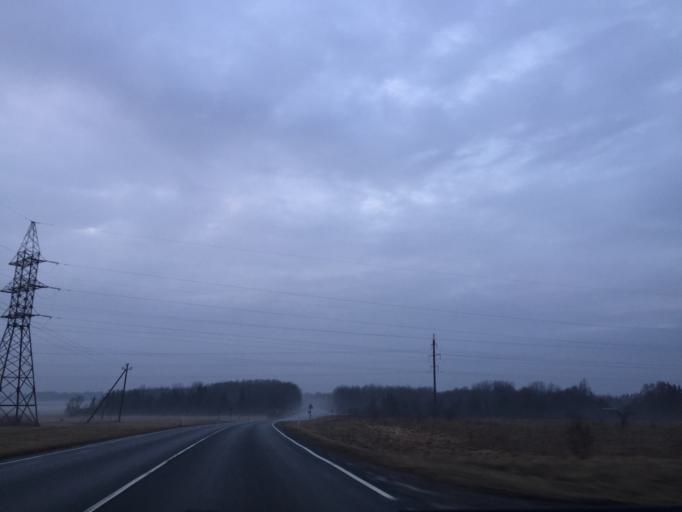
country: EE
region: Laeaene
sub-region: Lihula vald
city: Lihula
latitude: 58.6776
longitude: 23.8162
